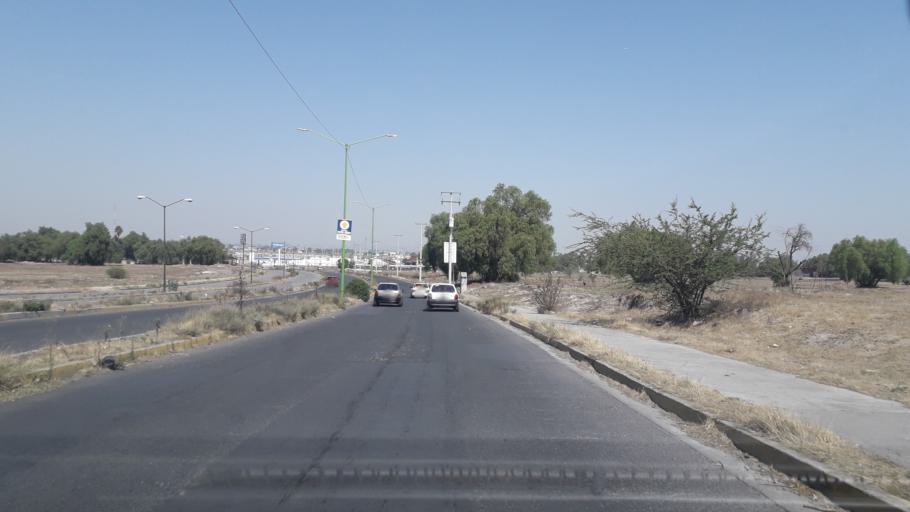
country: MX
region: Mexico
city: Santo Tomas Chiconautla
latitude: 19.6566
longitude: -99.0141
